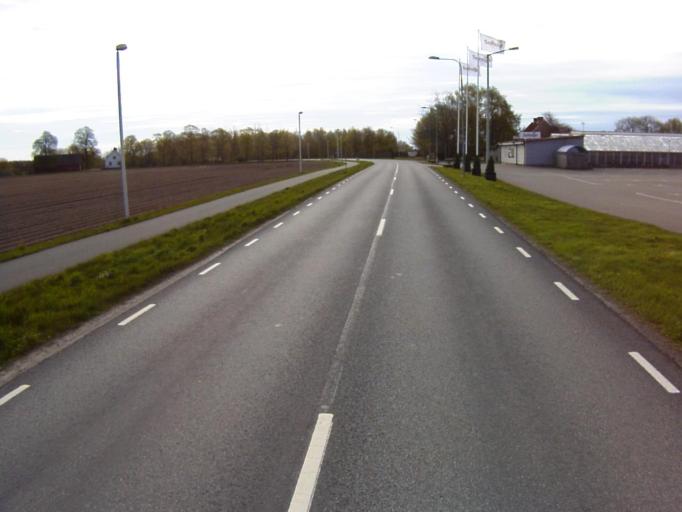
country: SE
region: Skane
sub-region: Kristianstads Kommun
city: Norra Asum
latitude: 56.0036
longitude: 14.1367
